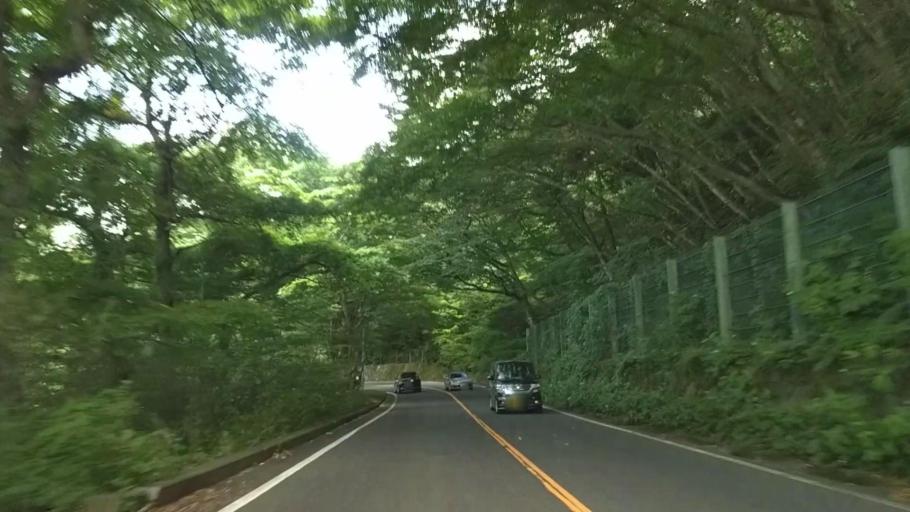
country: JP
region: Kanagawa
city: Hakone
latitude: 35.2352
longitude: 139.0004
